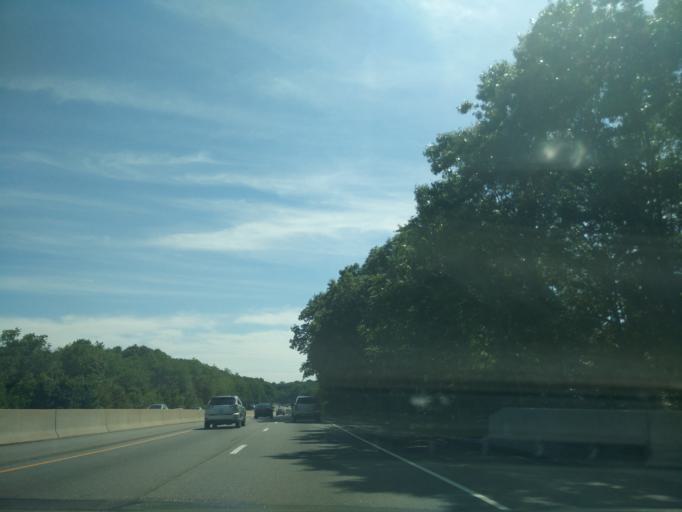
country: US
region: Connecticut
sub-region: New Haven County
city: Madison Center
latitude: 41.2878
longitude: -72.6121
